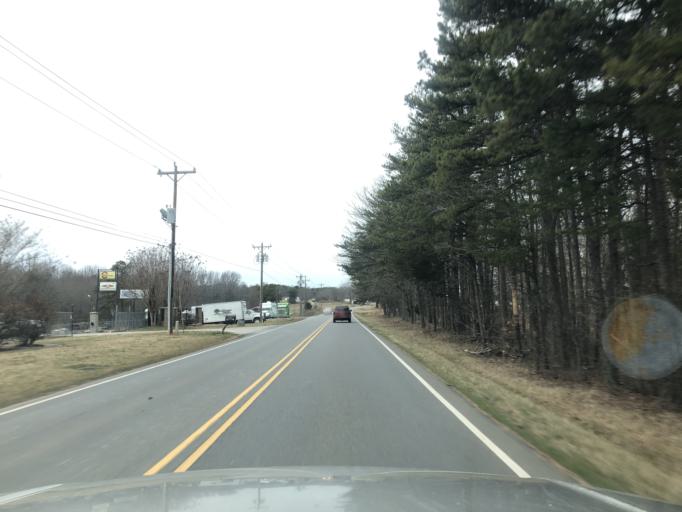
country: US
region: North Carolina
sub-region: Cleveland County
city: Shelby
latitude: 35.3332
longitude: -81.5002
